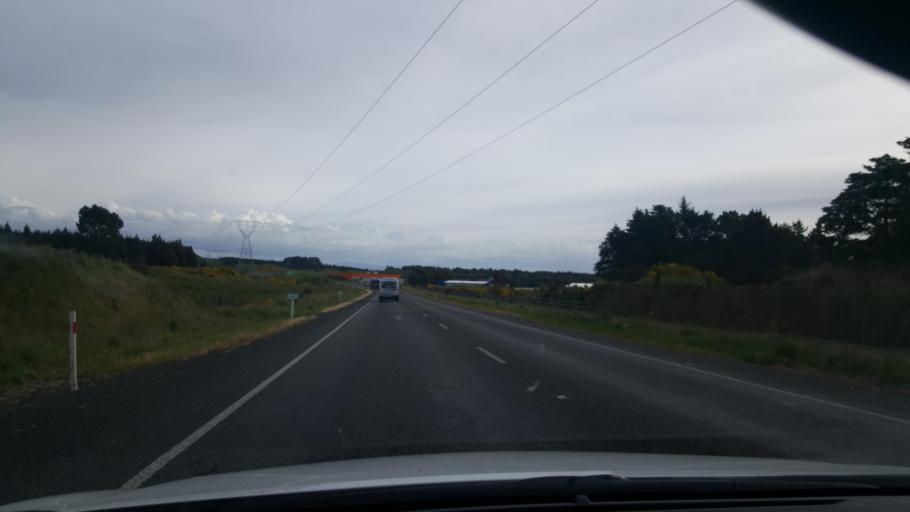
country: NZ
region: Waikato
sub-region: Taupo District
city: Taupo
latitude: -38.6968
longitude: 176.1130
